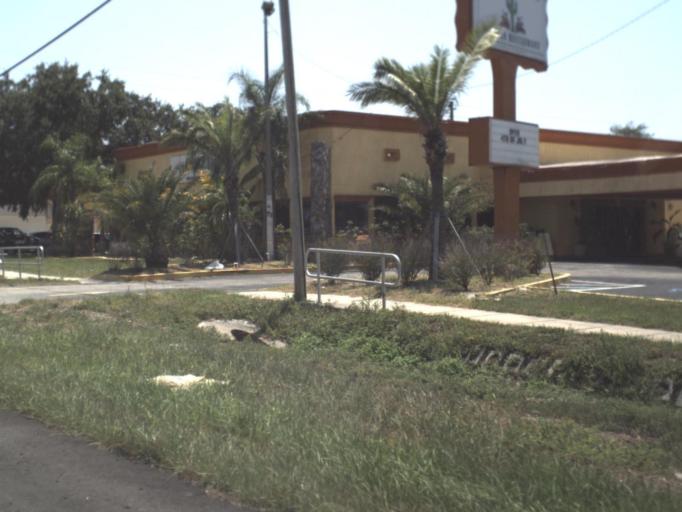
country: US
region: Florida
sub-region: Pinellas County
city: Tarpon Springs
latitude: 28.1261
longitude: -82.7403
